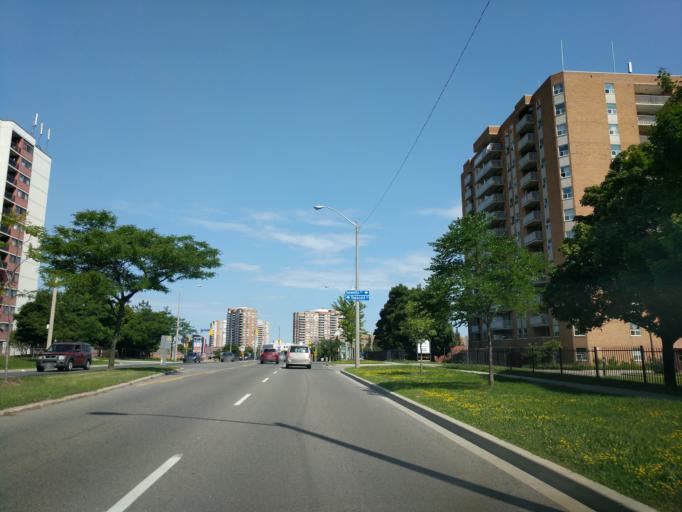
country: CA
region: Ontario
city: Scarborough
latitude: 43.8057
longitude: -79.2179
